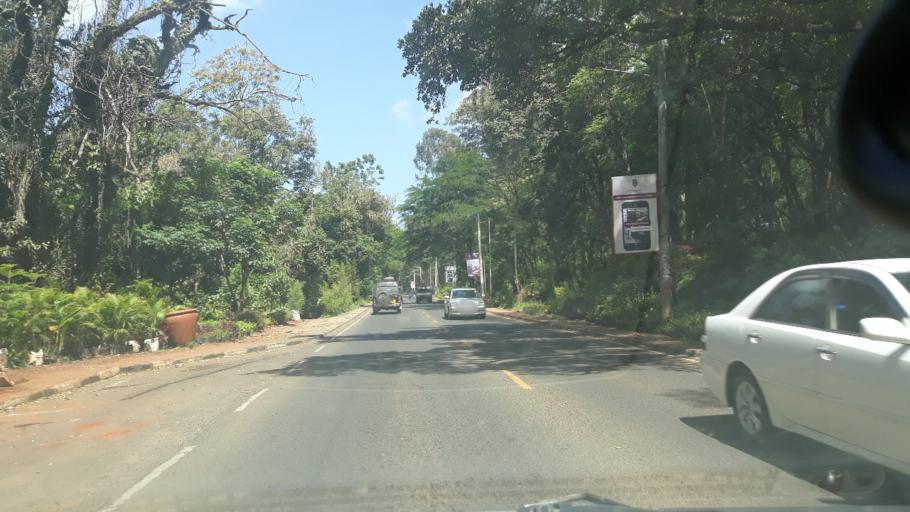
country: KE
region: Nairobi Area
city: Nairobi
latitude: -1.2469
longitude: 36.8157
